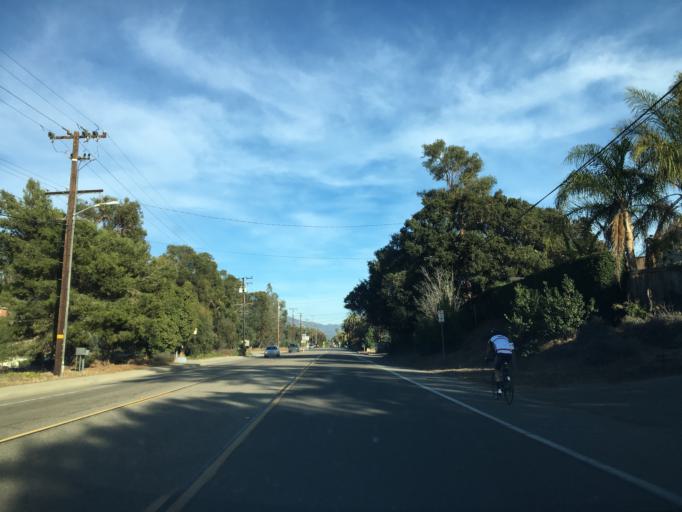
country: US
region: California
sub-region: Santa Barbara County
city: Goleta
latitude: 34.4386
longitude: -119.7785
